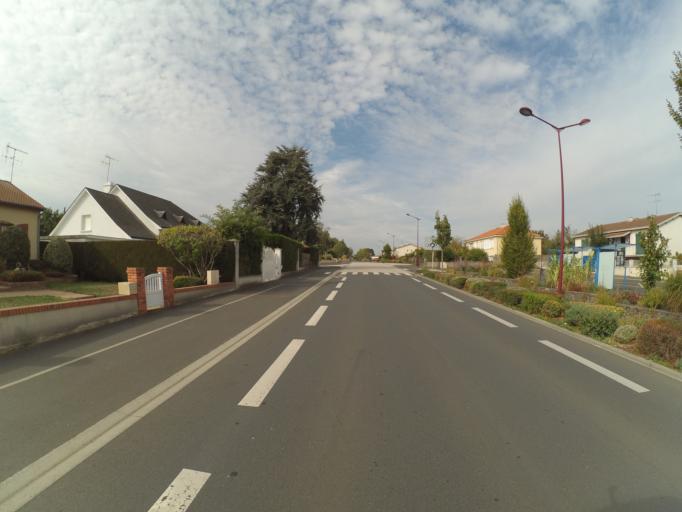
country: FR
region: Pays de la Loire
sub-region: Departement de Maine-et-Loire
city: Jallais
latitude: 47.1982
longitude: -0.8687
